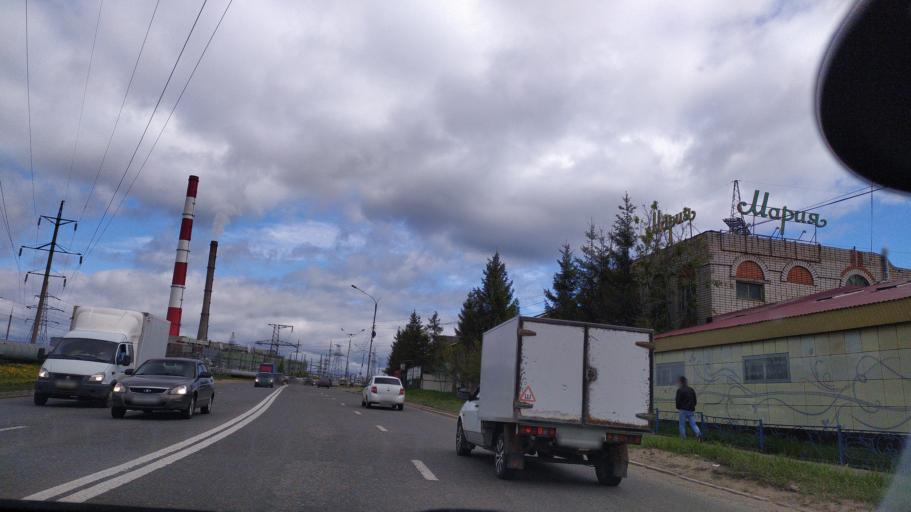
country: RU
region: Chuvashia
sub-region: Cheboksarskiy Rayon
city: Cheboksary
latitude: 56.1179
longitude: 47.3019
